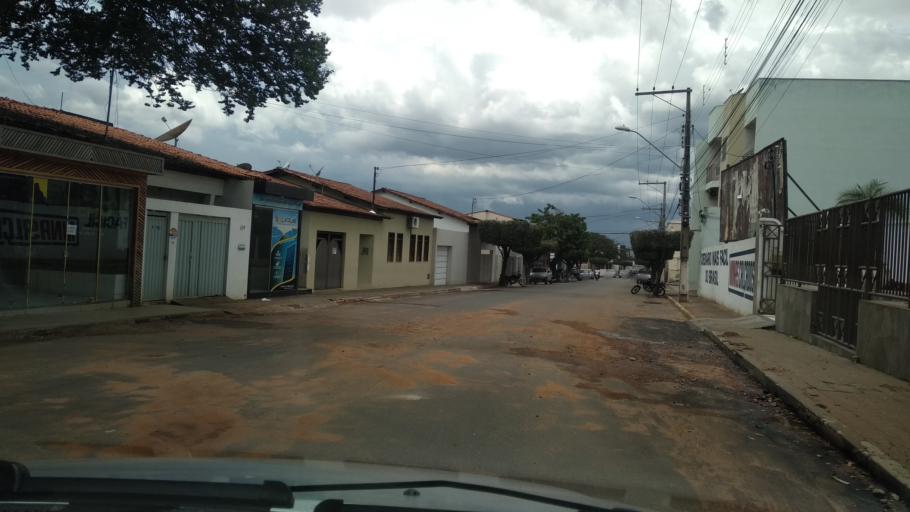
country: BR
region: Bahia
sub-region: Caetite
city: Caetite
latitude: -14.0704
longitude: -42.4911
